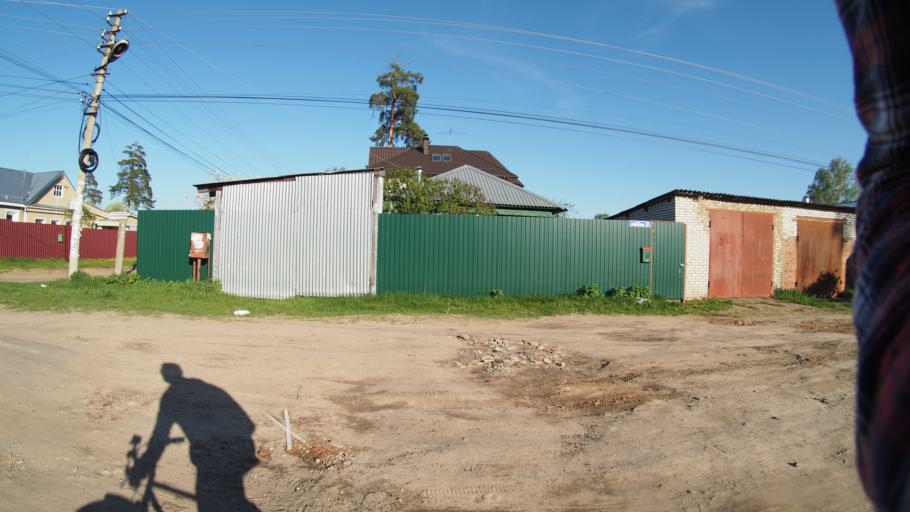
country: RU
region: Moskovskaya
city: Ramenskoye
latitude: 55.5601
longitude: 38.2000
